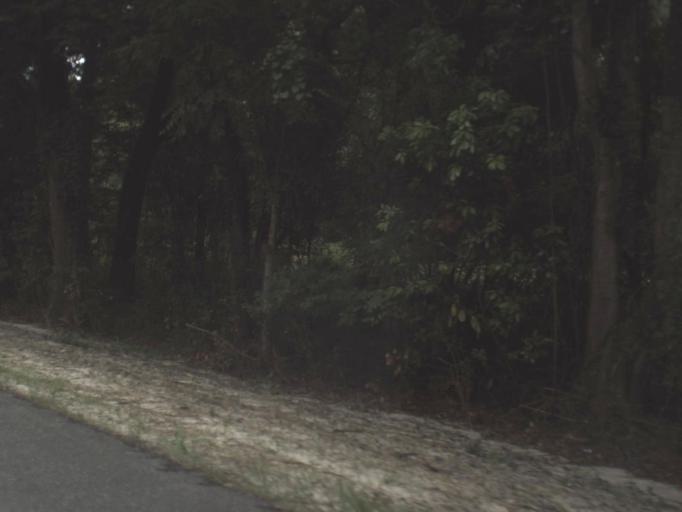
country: US
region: Florida
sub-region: Alachua County
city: Newberry
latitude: 29.5911
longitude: -82.5626
